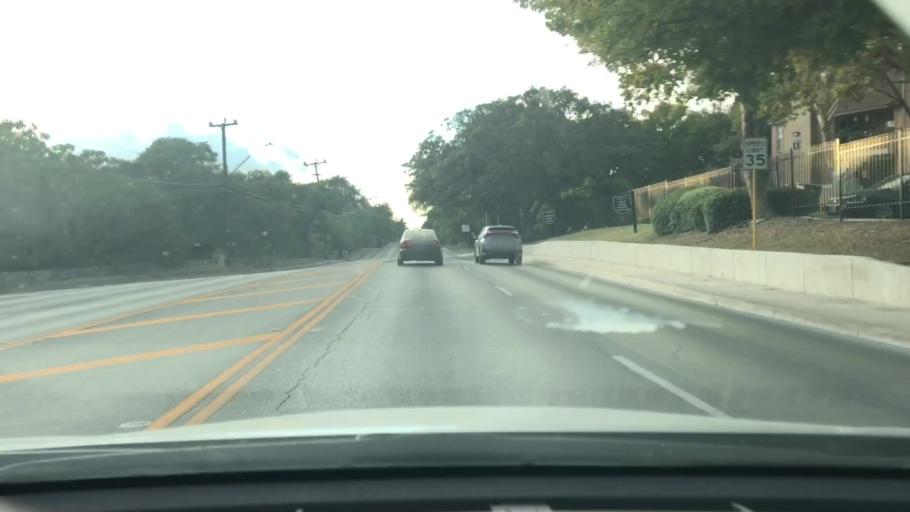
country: US
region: Texas
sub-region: Bexar County
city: Hollywood Park
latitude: 29.5576
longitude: -98.4731
